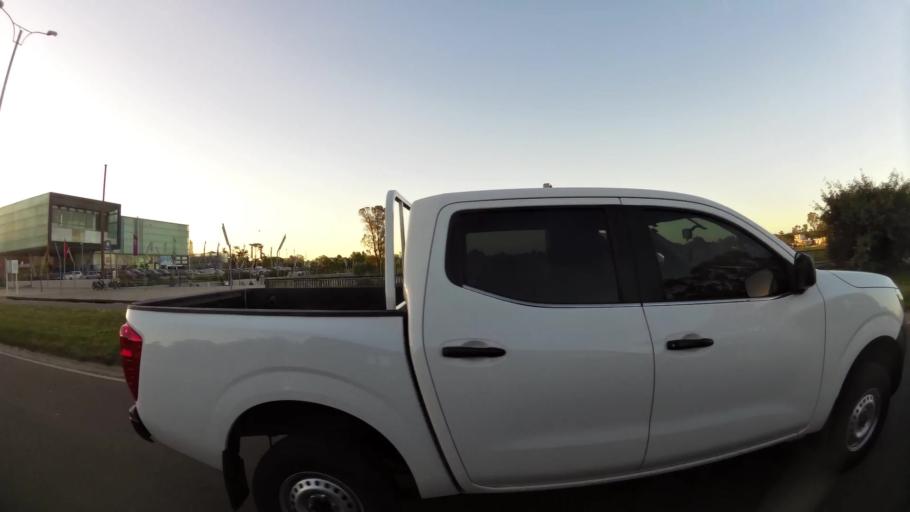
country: UY
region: Canelones
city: Barra de Carrasco
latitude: -34.8402
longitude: -55.9915
